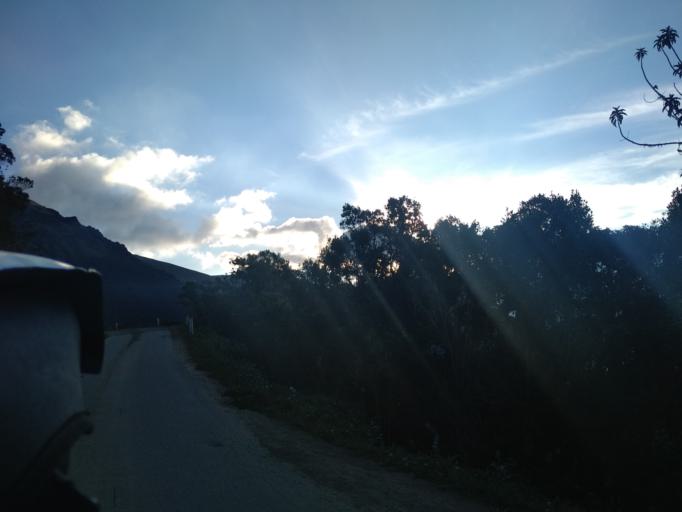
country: PE
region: Amazonas
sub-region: Provincia de Chachapoyas
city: Montevideo
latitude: -6.7125
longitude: -77.8711
